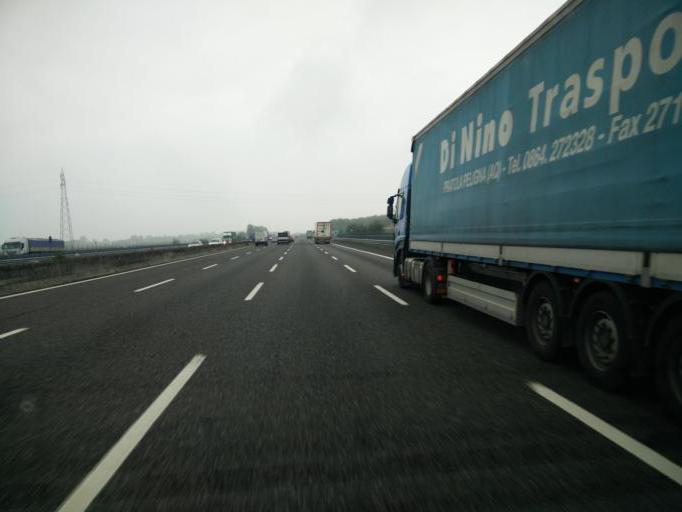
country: IT
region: Emilia-Romagna
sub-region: Provincia di Modena
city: Montale
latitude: 44.6095
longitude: 10.9061
